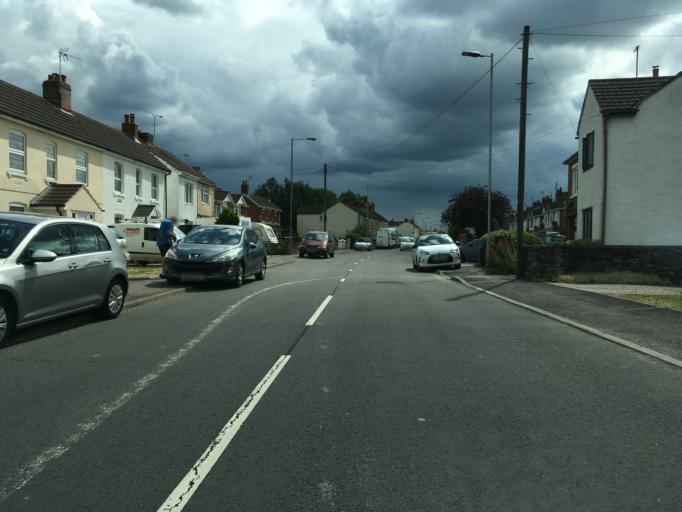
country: GB
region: England
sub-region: Borough of Swindon
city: Swindon
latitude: 51.5725
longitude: -1.7576
